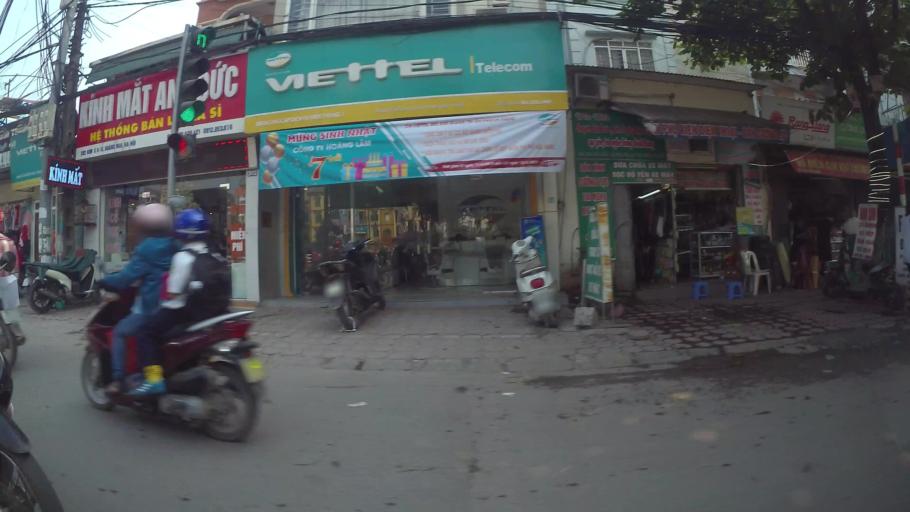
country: VN
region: Ha Noi
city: Thanh Xuan
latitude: 20.9800
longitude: 105.8189
